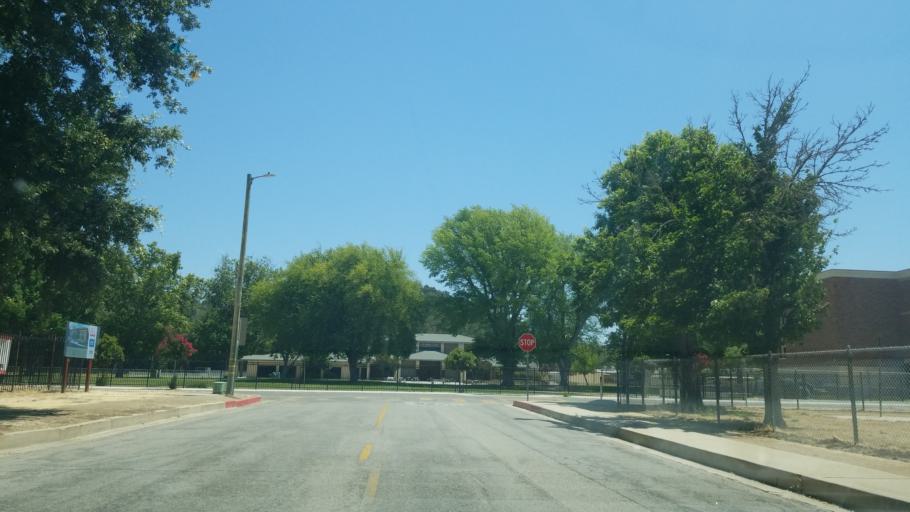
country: US
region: California
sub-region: San Luis Obispo County
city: Atascadero
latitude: 35.4919
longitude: -120.6668
